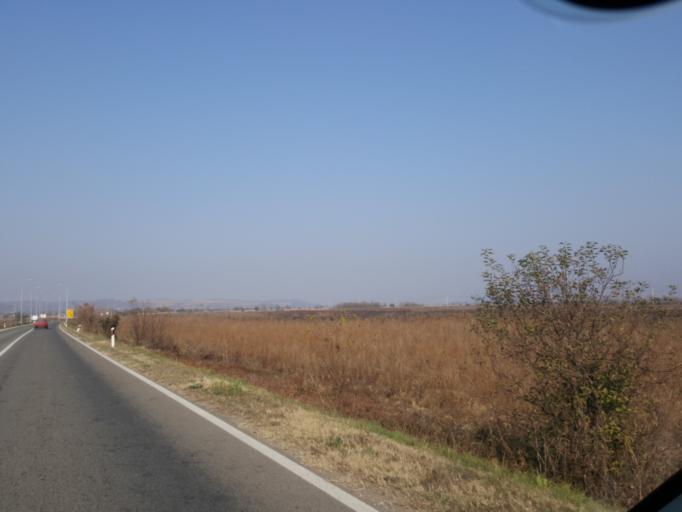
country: RS
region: Central Serbia
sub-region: Jablanicki Okrug
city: Leskovac
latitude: 43.0238
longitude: 21.9473
